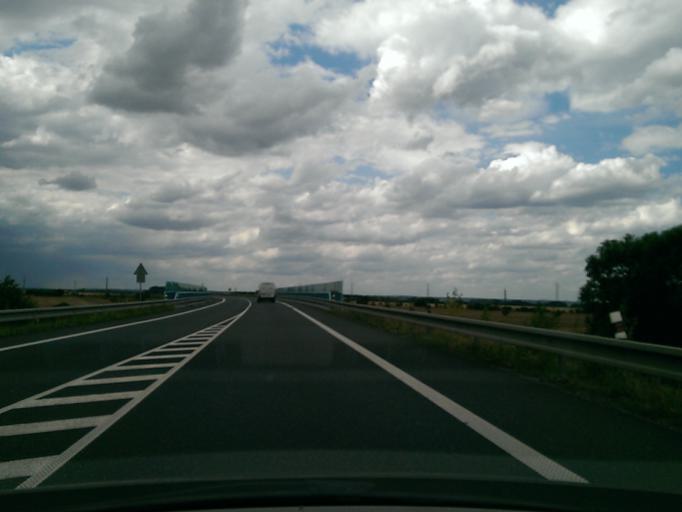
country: CZ
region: Central Bohemia
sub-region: Okres Nymburk
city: Nymburk
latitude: 50.1891
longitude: 15.0756
